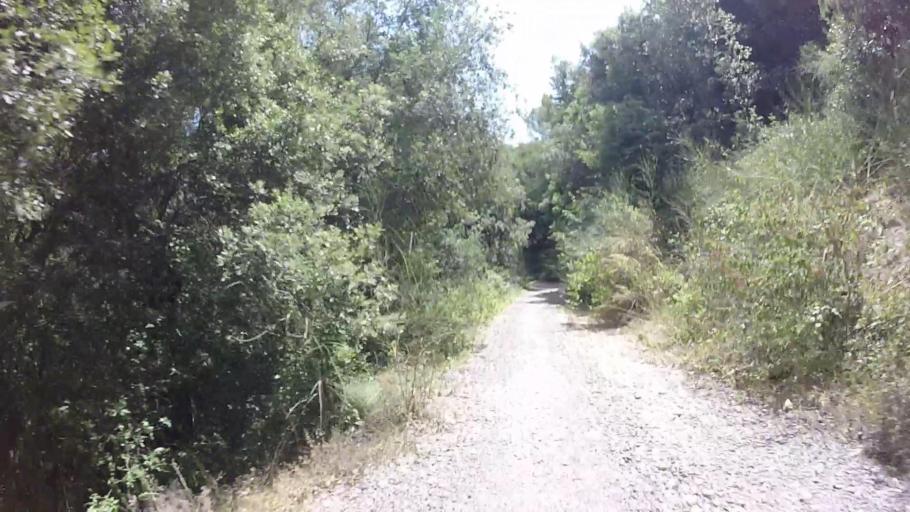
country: FR
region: Provence-Alpes-Cote d'Azur
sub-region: Departement des Alpes-Maritimes
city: Valbonne
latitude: 43.6201
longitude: 7.0260
